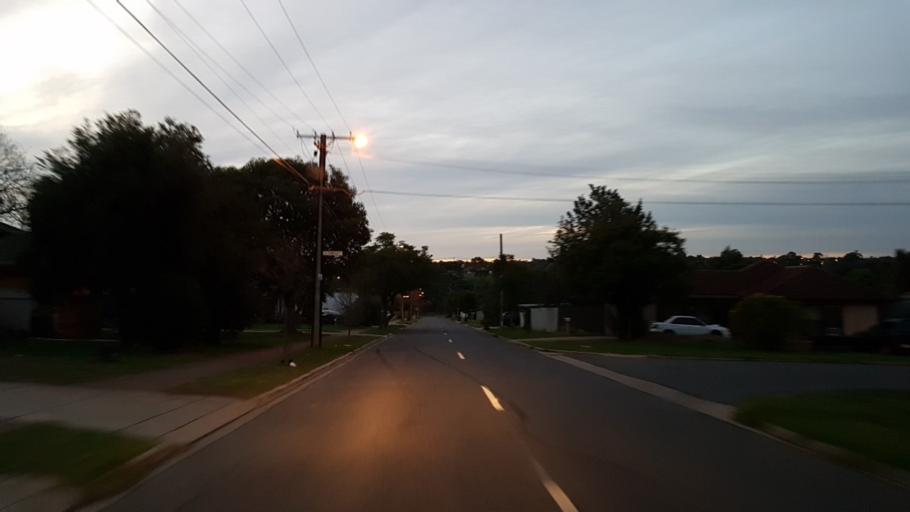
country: AU
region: South Australia
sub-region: Port Adelaide Enfield
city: Gilles Plains
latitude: -34.8485
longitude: 138.6641
